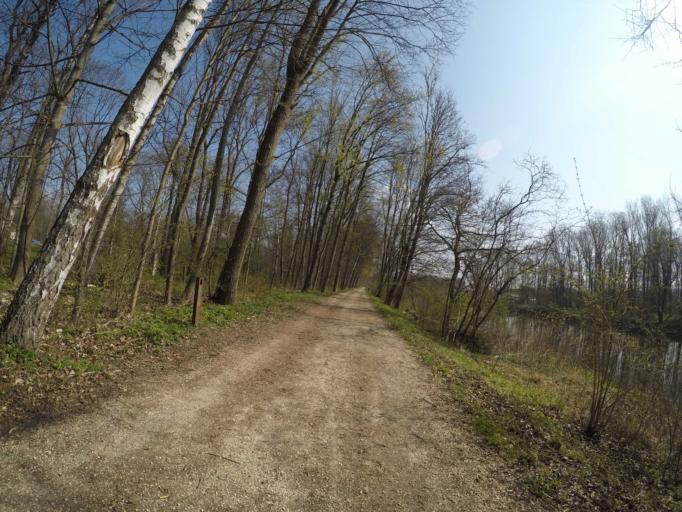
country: DE
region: Bavaria
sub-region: Swabia
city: Guenzburg
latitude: 48.4615
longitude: 10.2721
